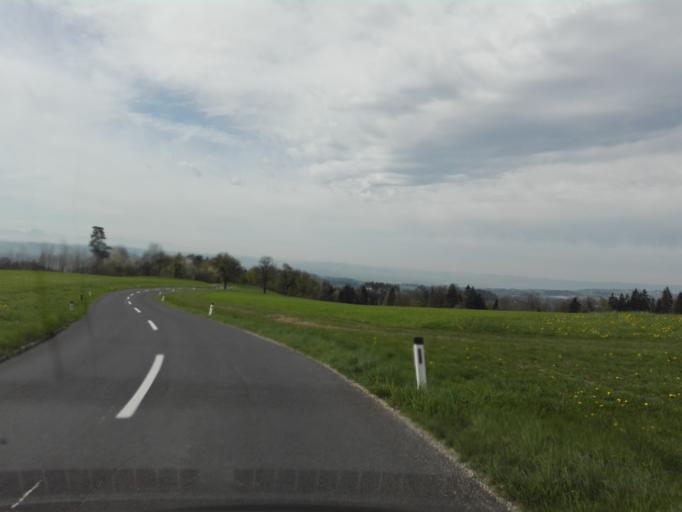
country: AT
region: Upper Austria
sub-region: Politischer Bezirk Urfahr-Umgebung
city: Gramastetten
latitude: 48.3735
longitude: 14.1793
